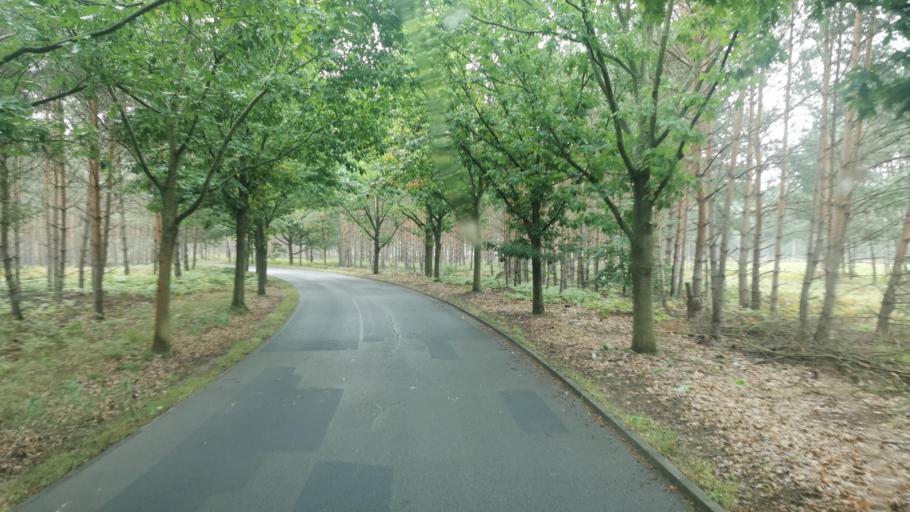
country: DE
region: Brandenburg
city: Kolkwitz
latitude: 51.7284
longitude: 14.2237
